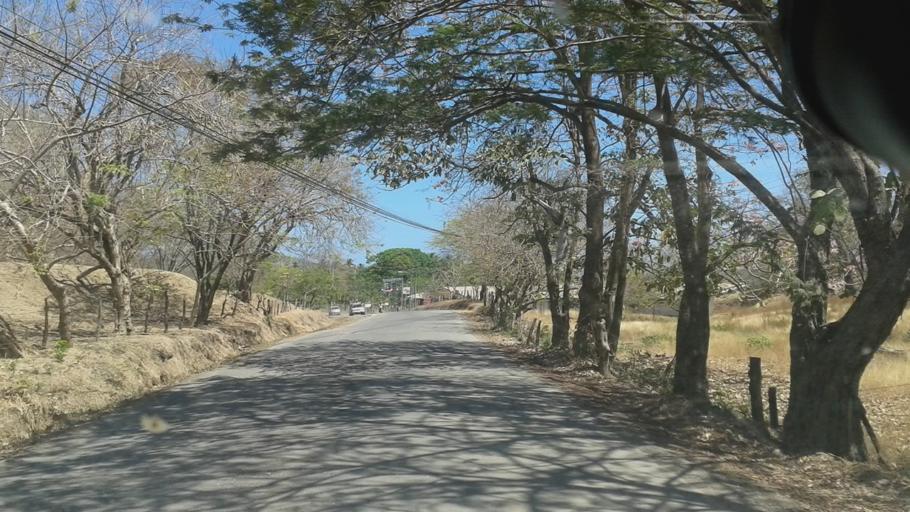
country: CR
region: Guanacaste
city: Samara
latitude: 9.9120
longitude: -85.6491
